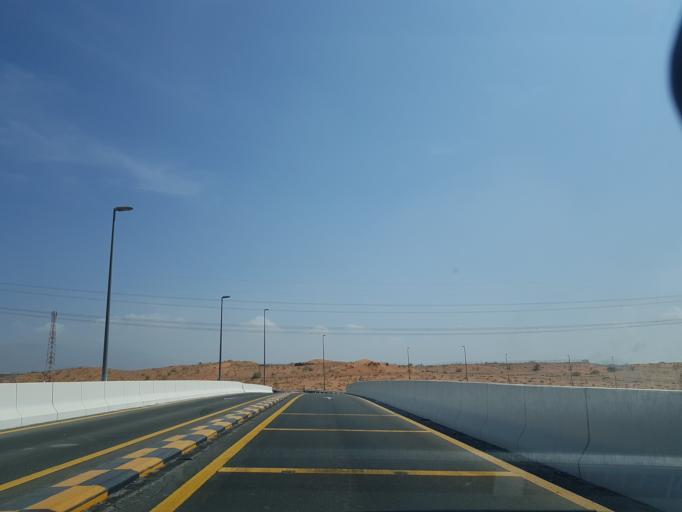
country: AE
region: Ra's al Khaymah
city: Ras al-Khaimah
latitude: 25.6661
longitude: 55.8951
